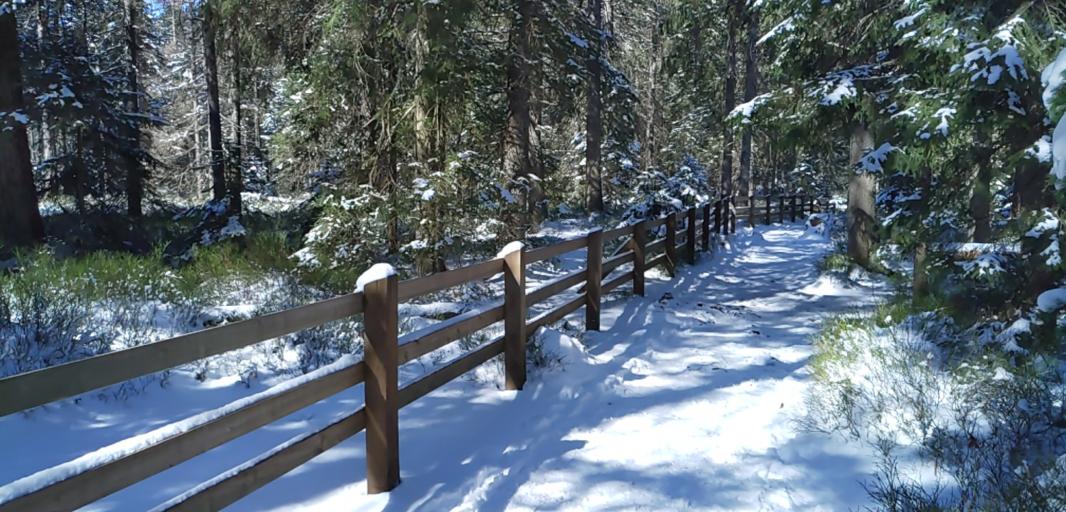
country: CH
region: Bern
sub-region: Jura bernois
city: Tramelan
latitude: 47.2406
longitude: 7.0507
